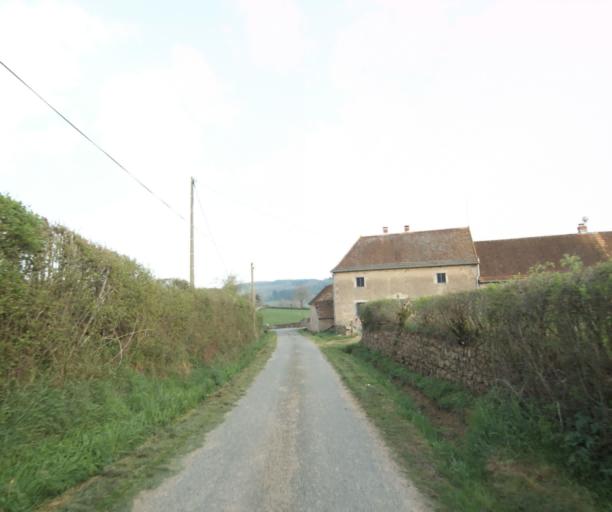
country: FR
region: Bourgogne
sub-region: Departement de Saone-et-Loire
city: Matour
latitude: 46.4271
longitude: 4.4644
